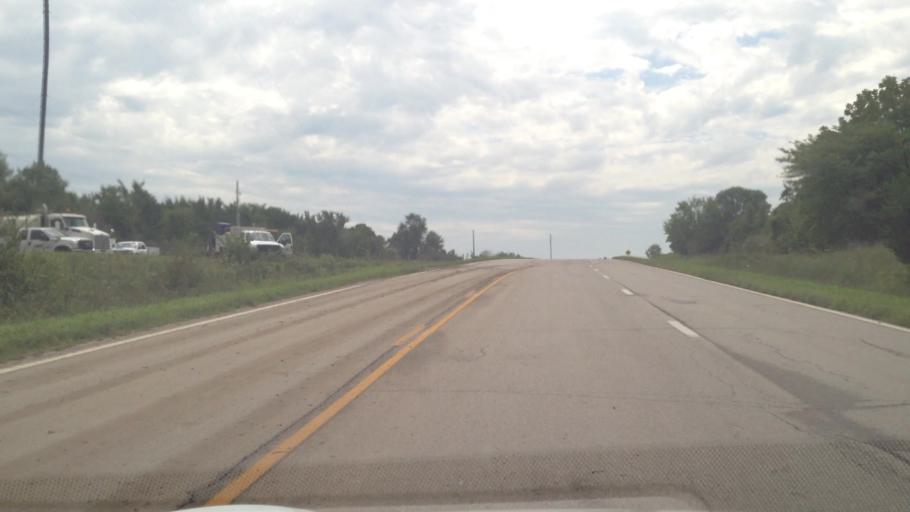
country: US
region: Kansas
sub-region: Bourbon County
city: Fort Scott
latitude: 37.8288
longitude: -94.9796
